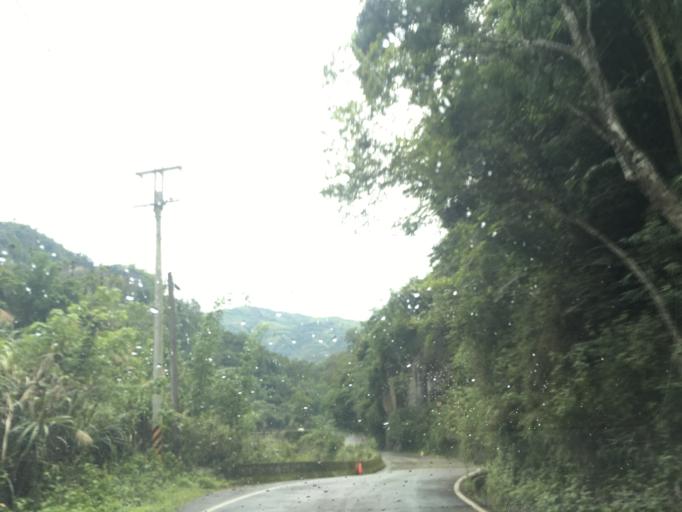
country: TW
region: Taiwan
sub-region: Yunlin
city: Douliu
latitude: 23.5661
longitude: 120.6408
